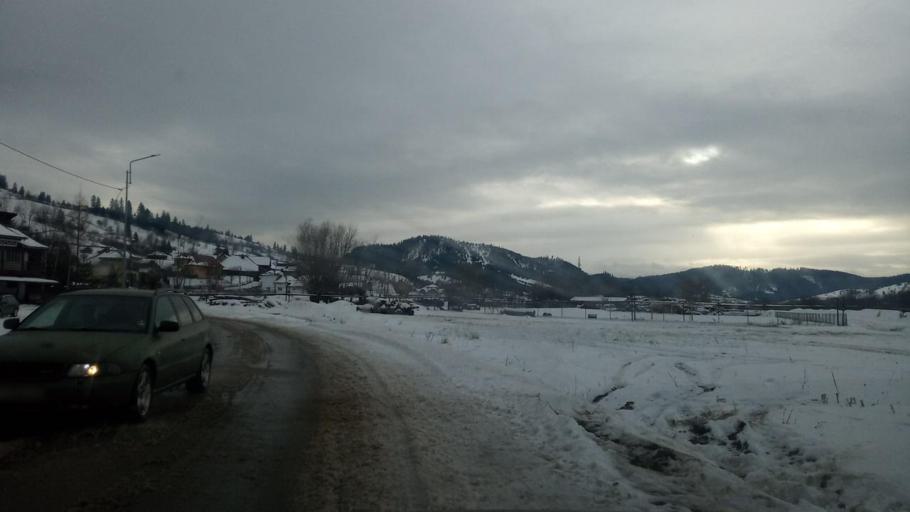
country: RO
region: Suceava
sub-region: Comuna Frasin
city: Plutonita
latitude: 47.5038
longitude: 25.7965
